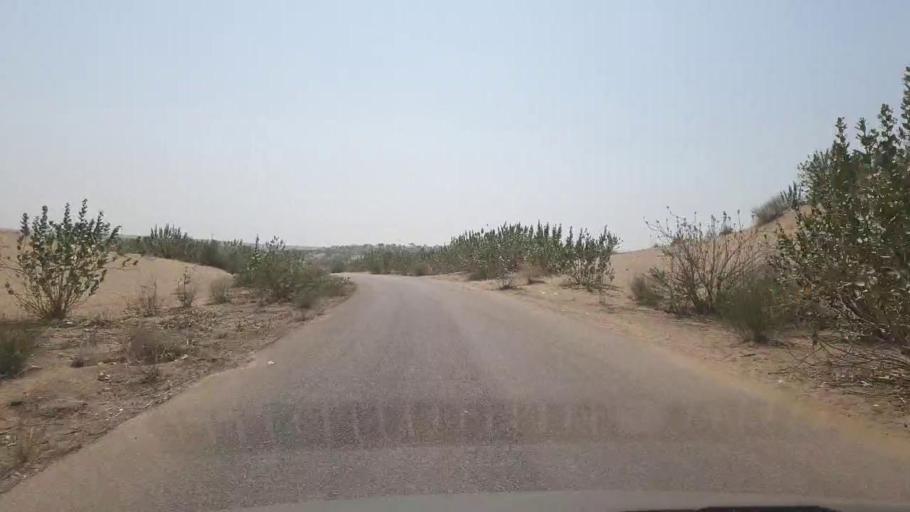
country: PK
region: Sindh
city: Chor
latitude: 25.6521
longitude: 70.1675
